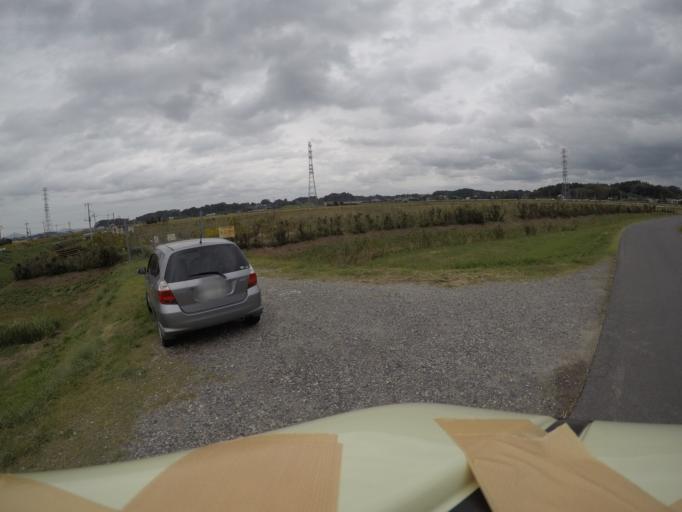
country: JP
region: Ibaraki
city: Ishioka
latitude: 36.1495
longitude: 140.3643
